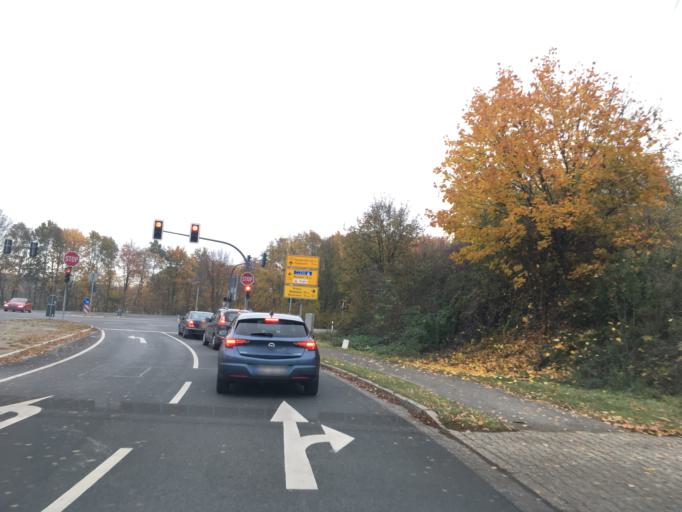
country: DE
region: North Rhine-Westphalia
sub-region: Regierungsbezirk Munster
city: Telgte
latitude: 51.9891
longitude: 7.7987
